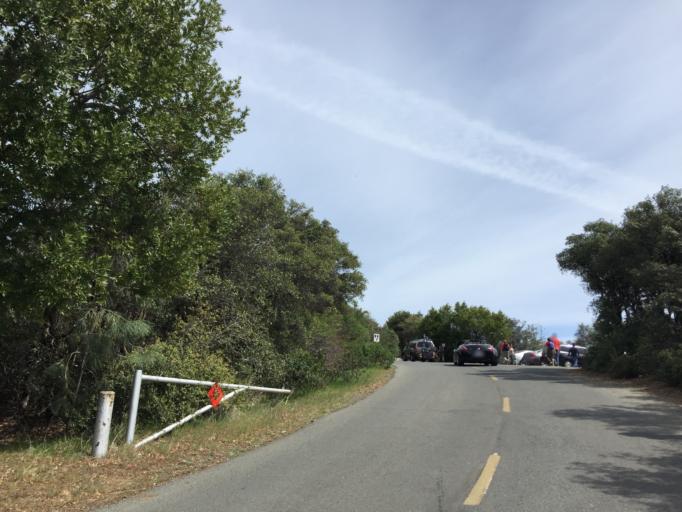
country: US
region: California
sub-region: Contra Costa County
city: Blackhawk
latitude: 37.8809
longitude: -121.9177
